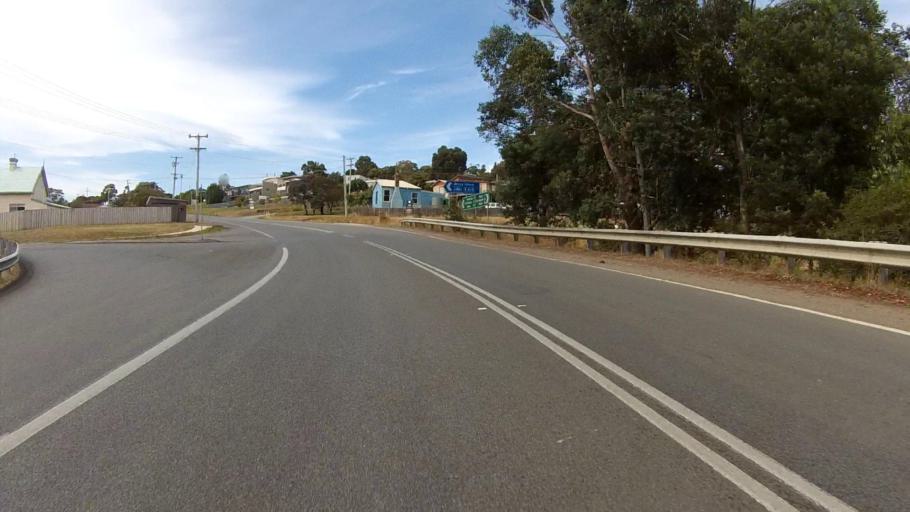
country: AU
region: Tasmania
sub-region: Kingborough
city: Kettering
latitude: -43.1278
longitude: 147.2465
